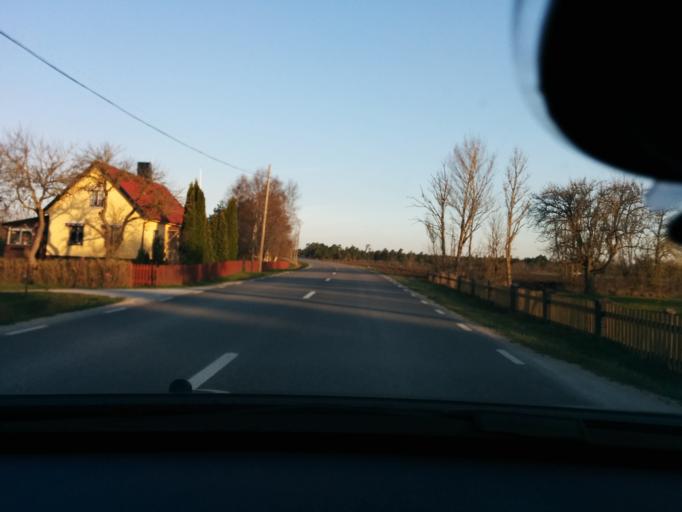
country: SE
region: Gotland
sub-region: Gotland
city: Visby
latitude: 57.6353
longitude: 18.5309
